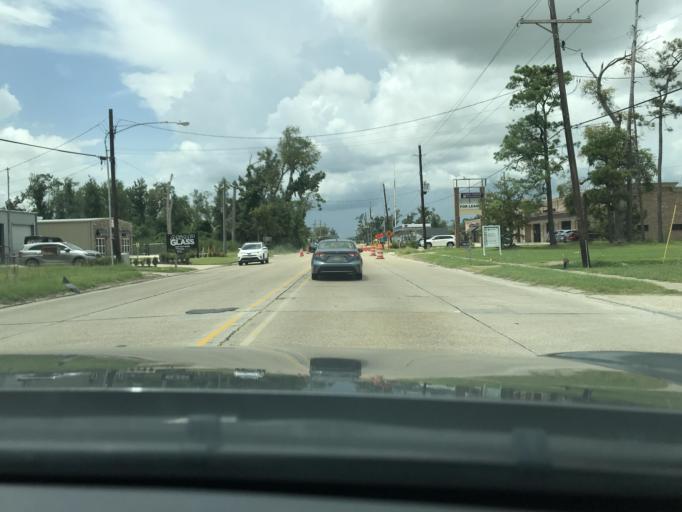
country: US
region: Louisiana
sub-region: Calcasieu Parish
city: Sulphur
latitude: 30.2276
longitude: -93.3374
